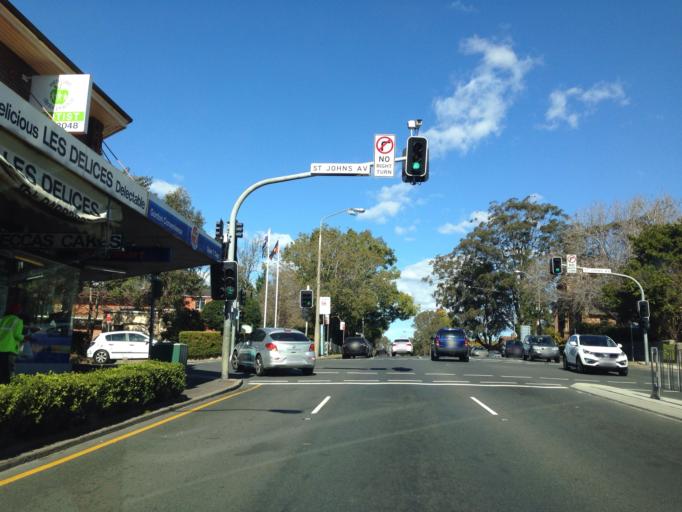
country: AU
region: New South Wales
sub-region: Ku-ring-gai
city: Killara
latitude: -33.7562
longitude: 151.1530
